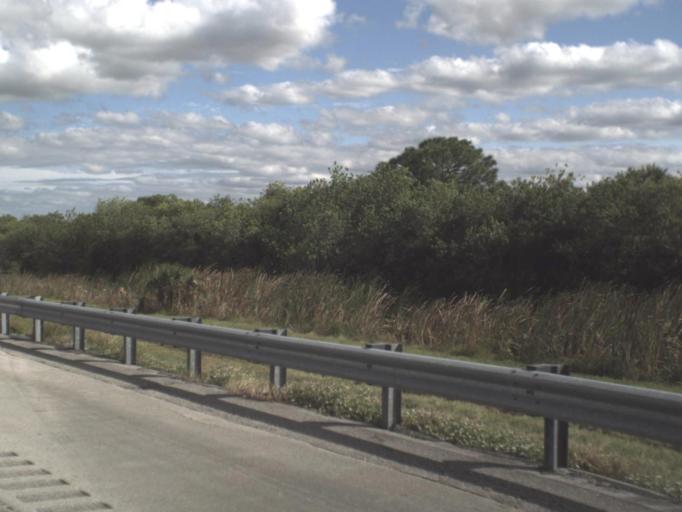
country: US
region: Florida
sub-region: Saint Lucie County
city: Lakewood Park
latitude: 27.4850
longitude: -80.5437
